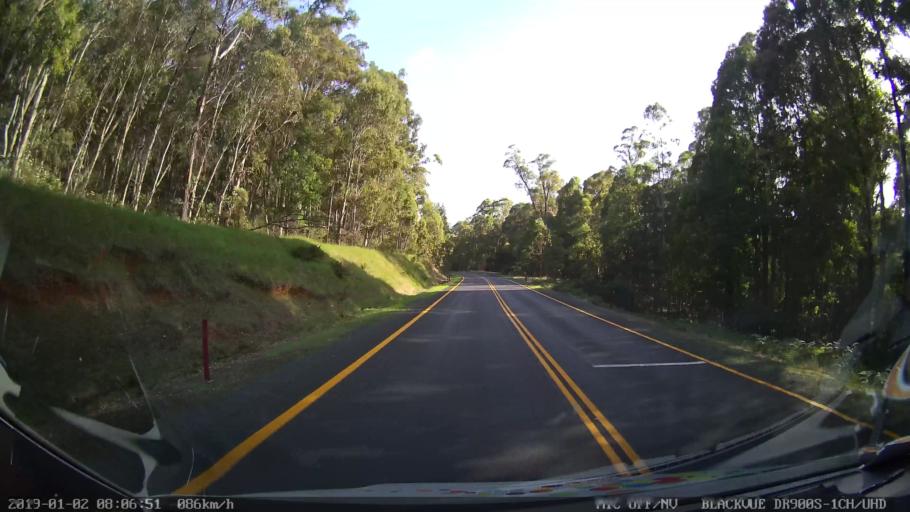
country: AU
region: New South Wales
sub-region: Tumut Shire
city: Tumut
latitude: -35.6351
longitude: 148.3877
